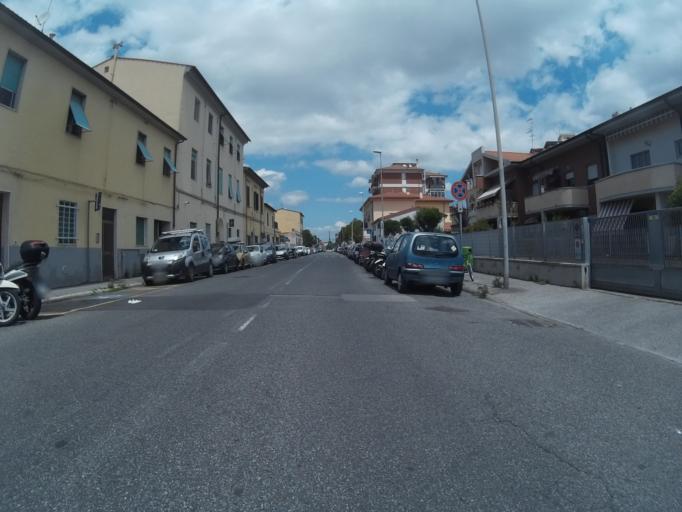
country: IT
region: Tuscany
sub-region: Provincia di Livorno
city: Livorno
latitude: 43.5639
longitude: 10.3305
